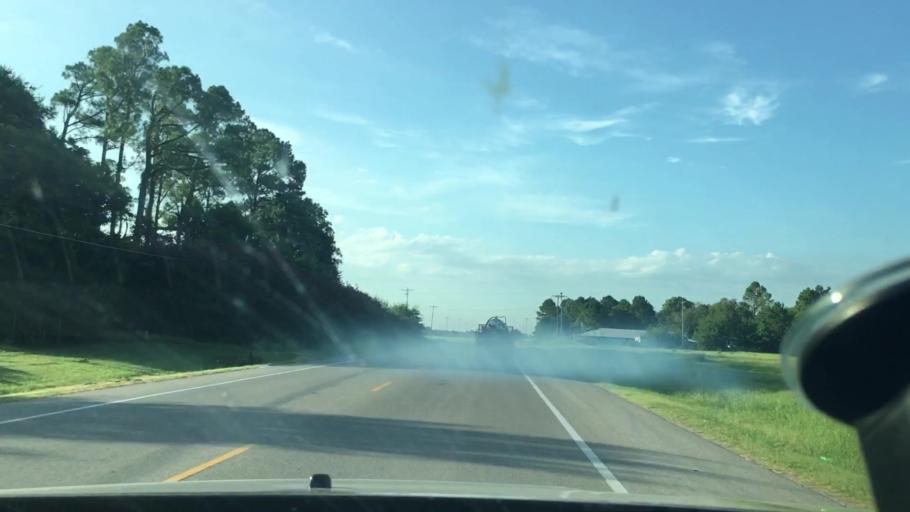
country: US
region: Oklahoma
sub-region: Garvin County
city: Wynnewood
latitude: 34.6679
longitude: -97.2054
